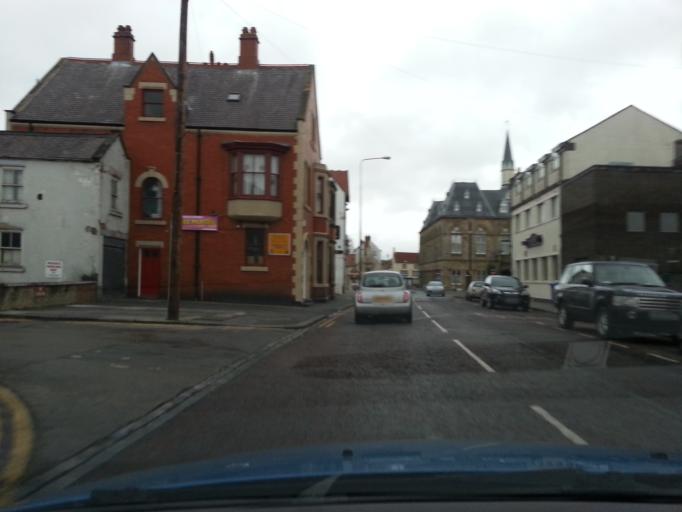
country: GB
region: England
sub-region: County Durham
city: Bishop Auckland
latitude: 54.6658
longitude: -1.6753
